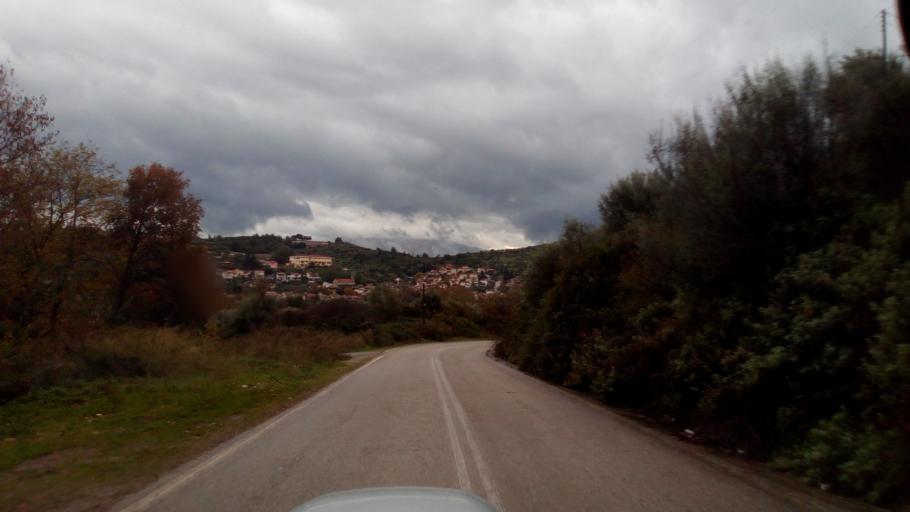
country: GR
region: West Greece
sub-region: Nomos Aitolias kai Akarnanias
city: Nafpaktos
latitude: 38.4263
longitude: 21.9300
